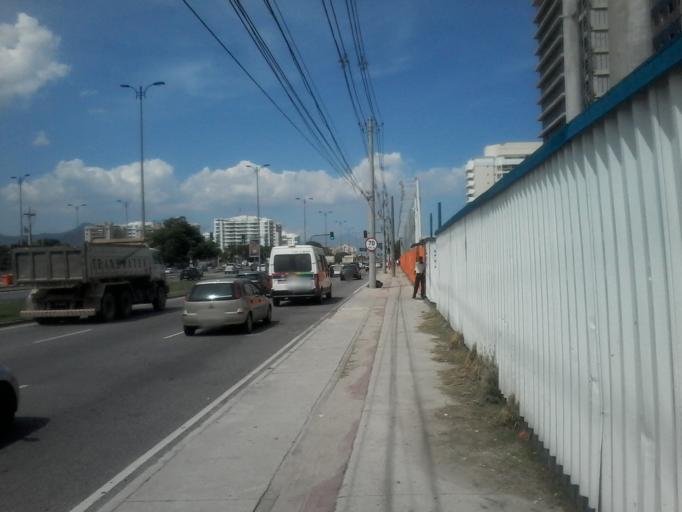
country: BR
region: Rio de Janeiro
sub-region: Nilopolis
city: Nilopolis
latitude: -23.0200
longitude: -43.4871
